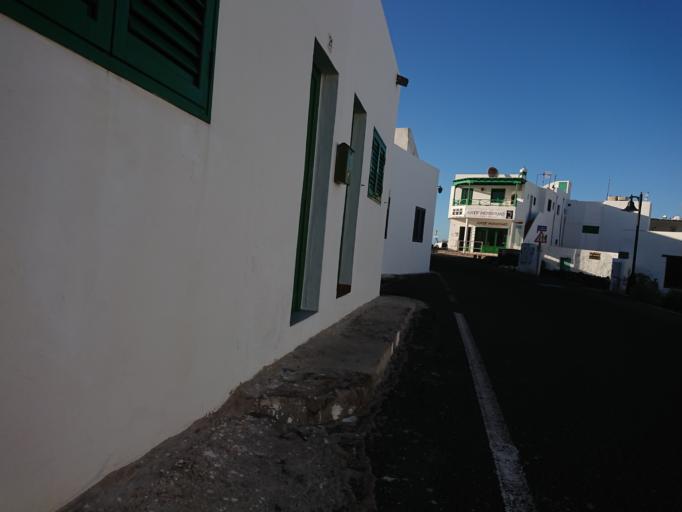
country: ES
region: Canary Islands
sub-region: Provincia de Las Palmas
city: Yaiza
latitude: 28.9818
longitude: -13.8312
